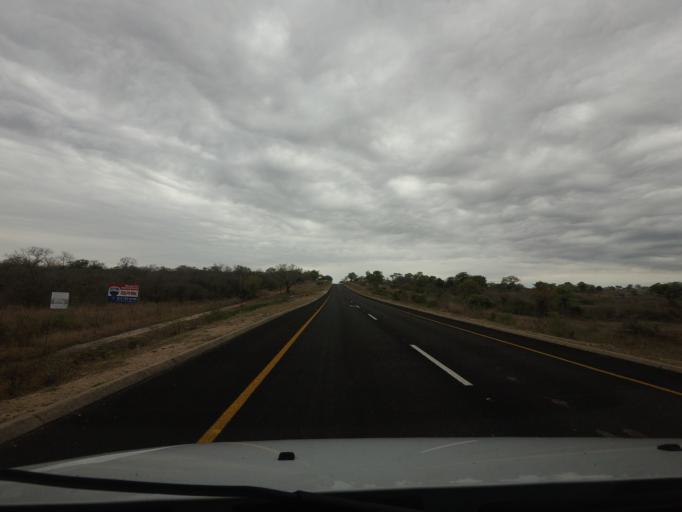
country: ZA
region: Limpopo
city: Thulamahashi
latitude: -24.5666
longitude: 31.1013
